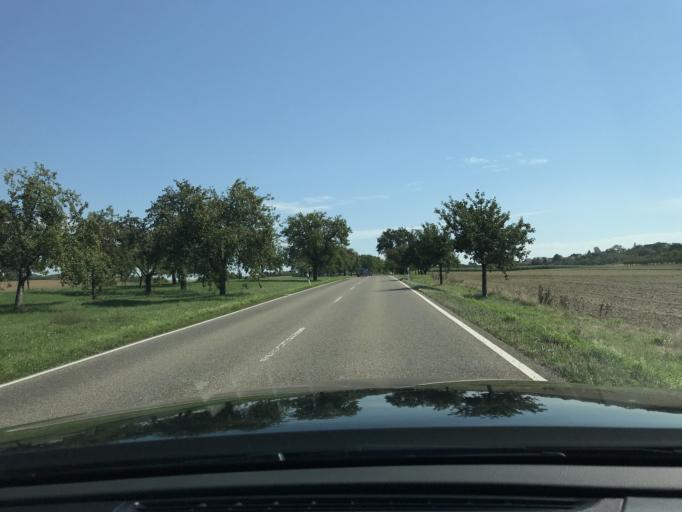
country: DE
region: Baden-Wuerttemberg
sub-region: Regierungsbezirk Stuttgart
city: Erdmannhausen
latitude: 48.9272
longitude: 9.3068
